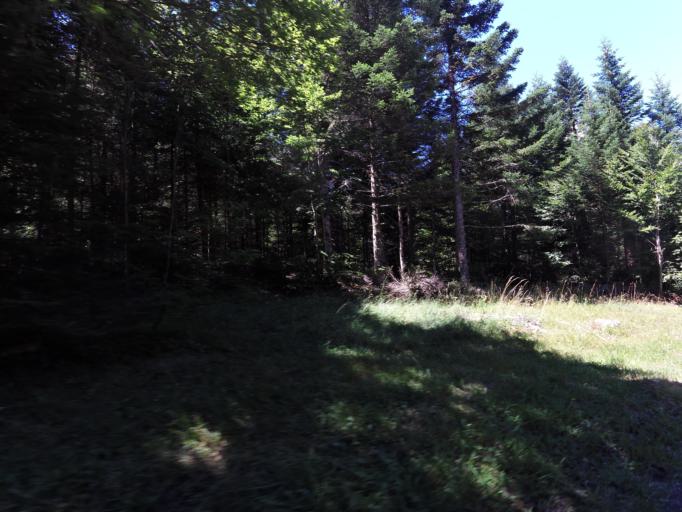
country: FR
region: Languedoc-Roussillon
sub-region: Departement de la Lozere
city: Meyrueis
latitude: 44.1037
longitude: 3.5167
